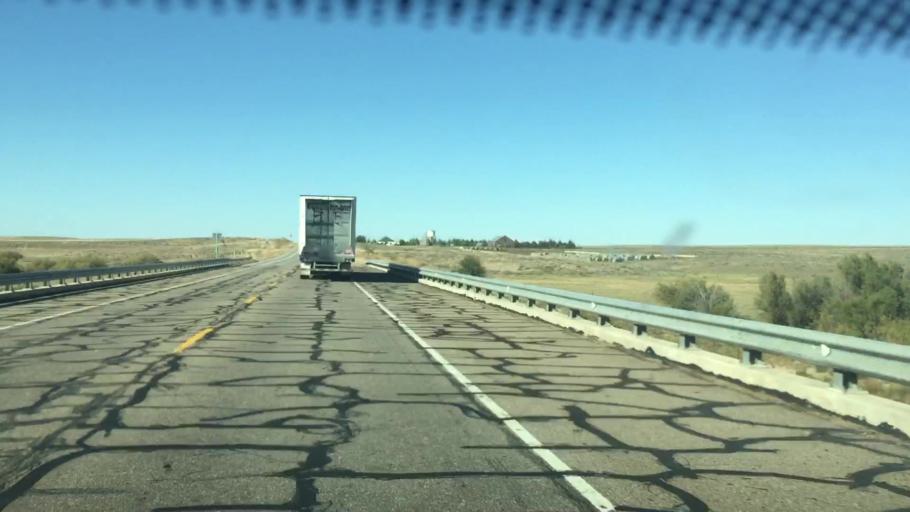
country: US
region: Colorado
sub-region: Kiowa County
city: Eads
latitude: 38.6121
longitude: -102.7857
